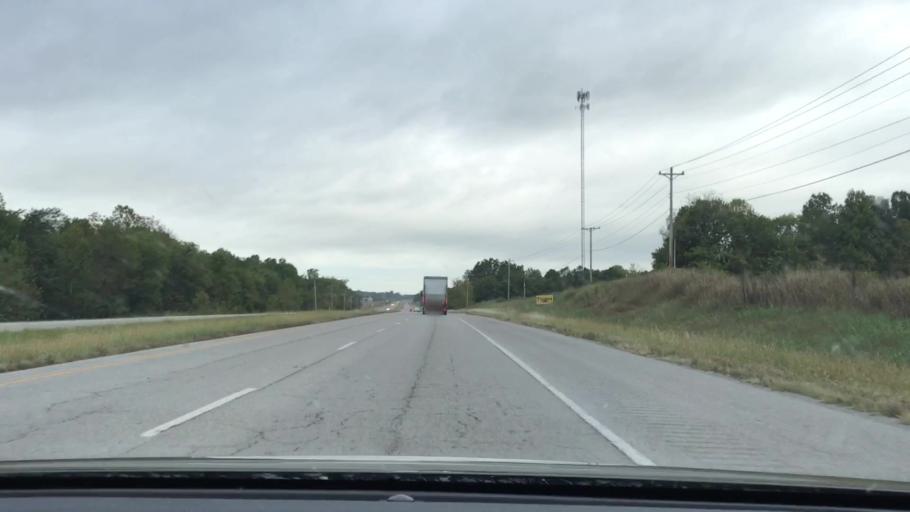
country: US
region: Kentucky
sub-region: Christian County
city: Hopkinsville
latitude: 36.8308
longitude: -87.5204
